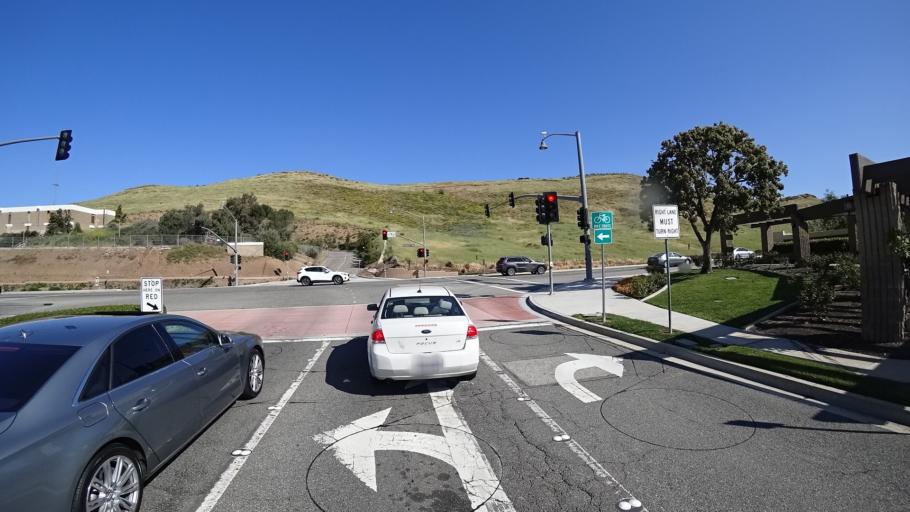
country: US
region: California
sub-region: Ventura County
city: Simi Valley
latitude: 34.2513
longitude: -118.8220
